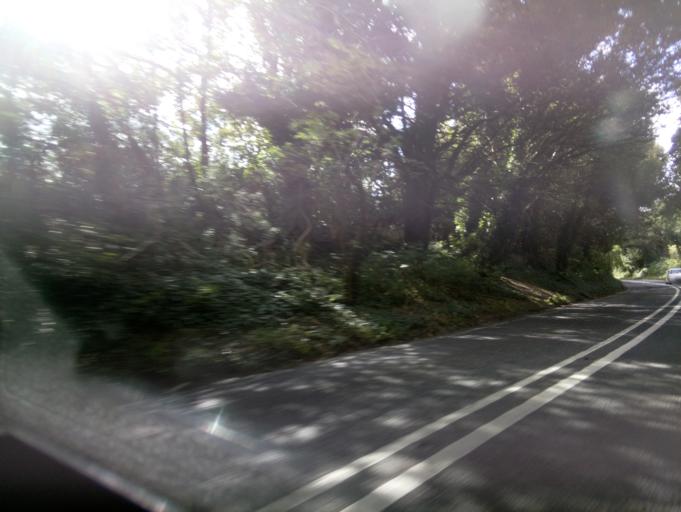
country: GB
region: England
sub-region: Hampshire
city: Abbotts Ann
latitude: 51.1129
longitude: -1.5666
